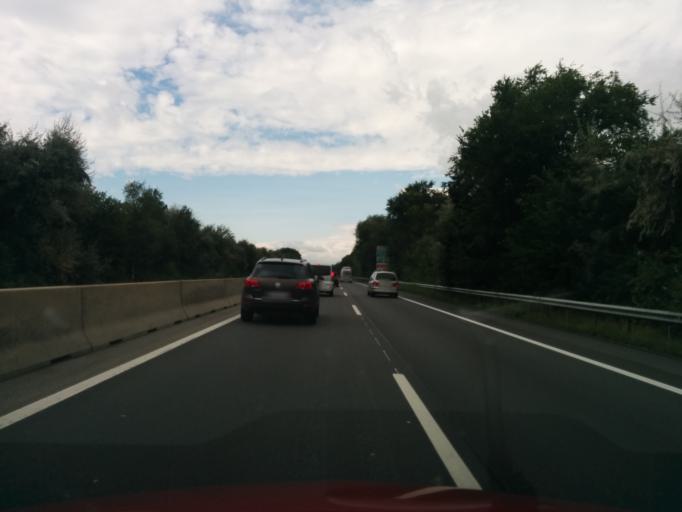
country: AT
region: Lower Austria
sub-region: Politischer Bezirk Bruck an der Leitha
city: Bruck an der Leitha
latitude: 48.0519
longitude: 16.7293
